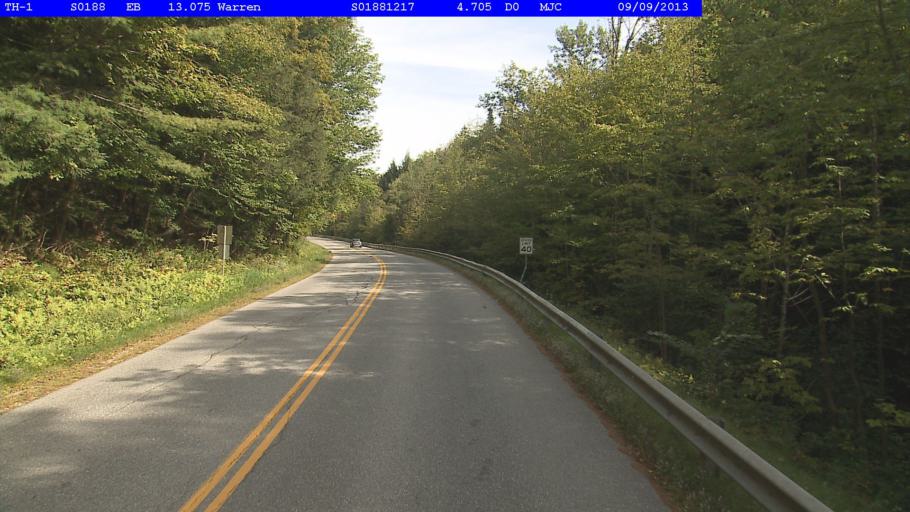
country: US
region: Vermont
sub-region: Washington County
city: Northfield
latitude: 44.1119
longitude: -72.8483
